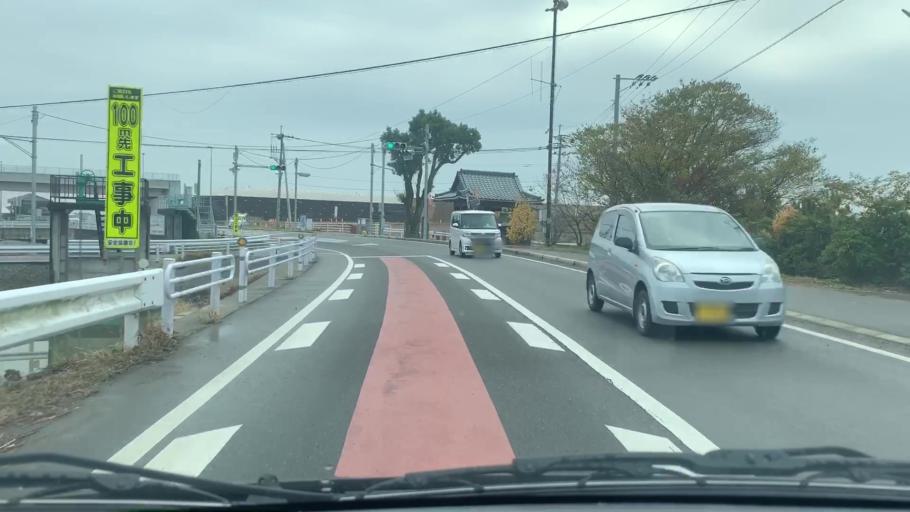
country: JP
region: Saga Prefecture
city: Saga-shi
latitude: 33.2033
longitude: 130.2134
